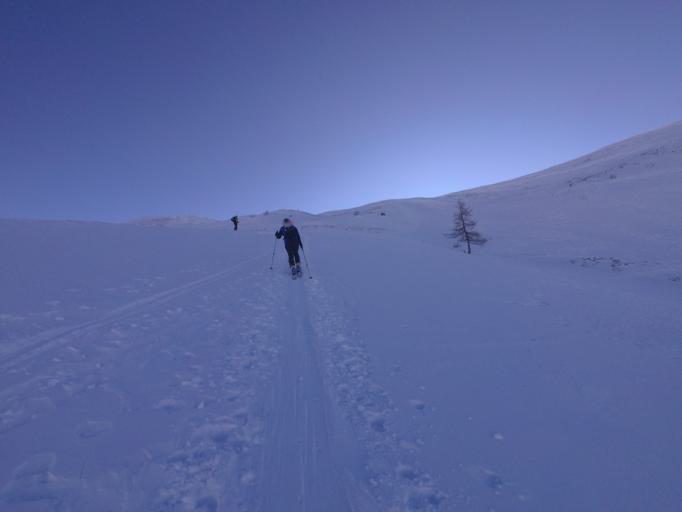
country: AT
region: Salzburg
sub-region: Politischer Bezirk Sankt Johann im Pongau
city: Huttschlag
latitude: 47.1751
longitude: 13.3011
